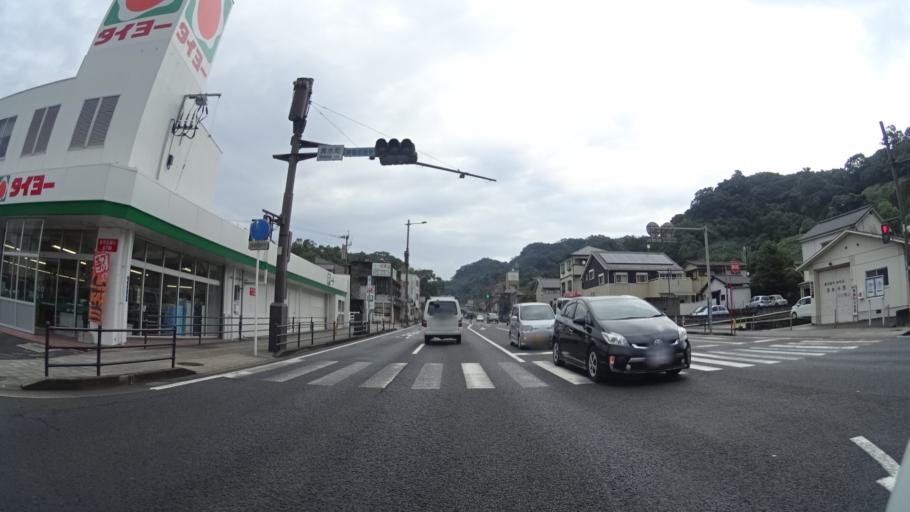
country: JP
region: Kagoshima
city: Kagoshima-shi
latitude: 31.6080
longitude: 130.5685
